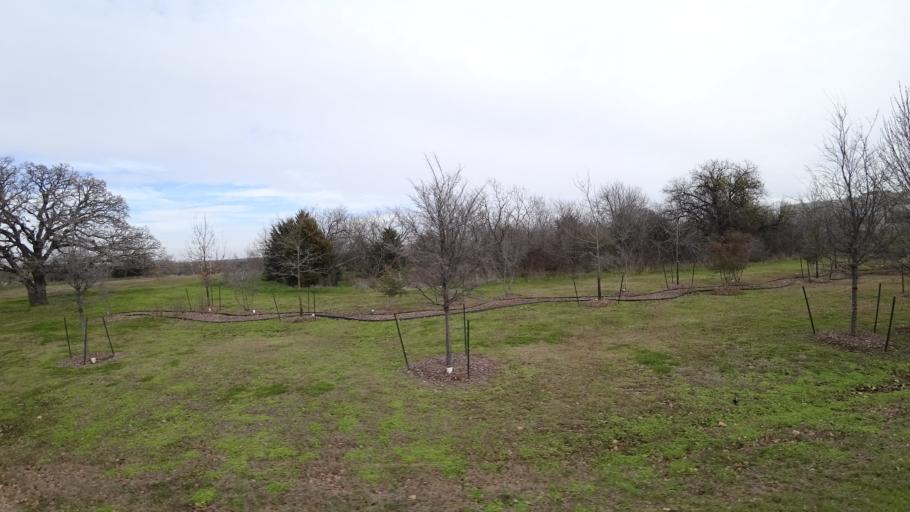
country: US
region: Texas
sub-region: Denton County
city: Lewisville
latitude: 33.0308
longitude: -96.9875
